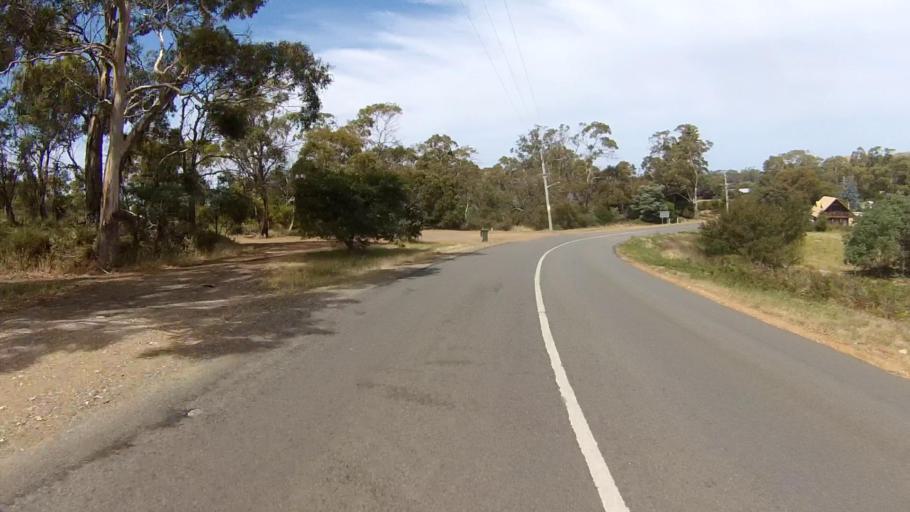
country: AU
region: Tasmania
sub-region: Kingborough
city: Taroona
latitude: -43.0175
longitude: 147.4182
